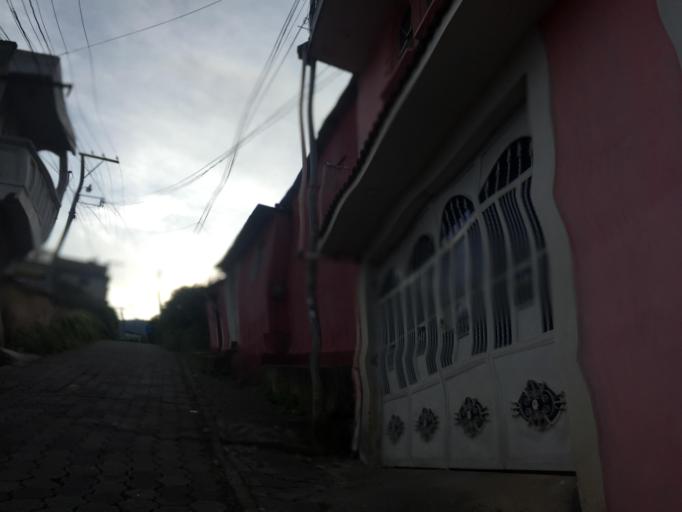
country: GT
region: Totonicapan
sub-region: Municipio de Totonicapan
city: Totonicapan
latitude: 14.9125
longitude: -91.3545
